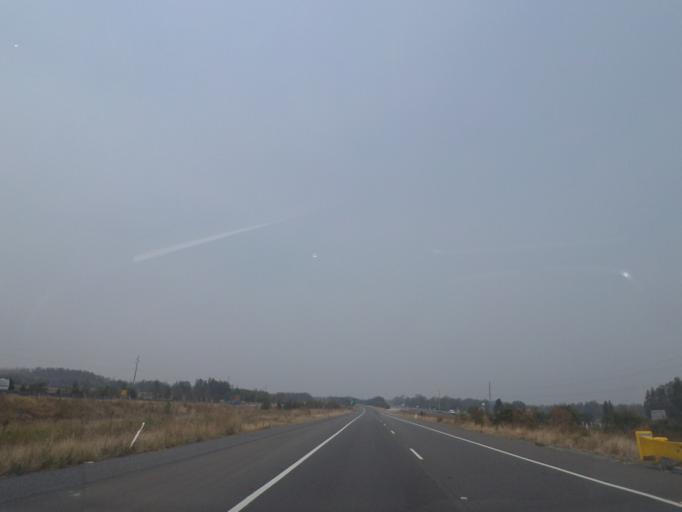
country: AU
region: New South Wales
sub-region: Ballina
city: Ballina
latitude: -28.8653
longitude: 153.5042
